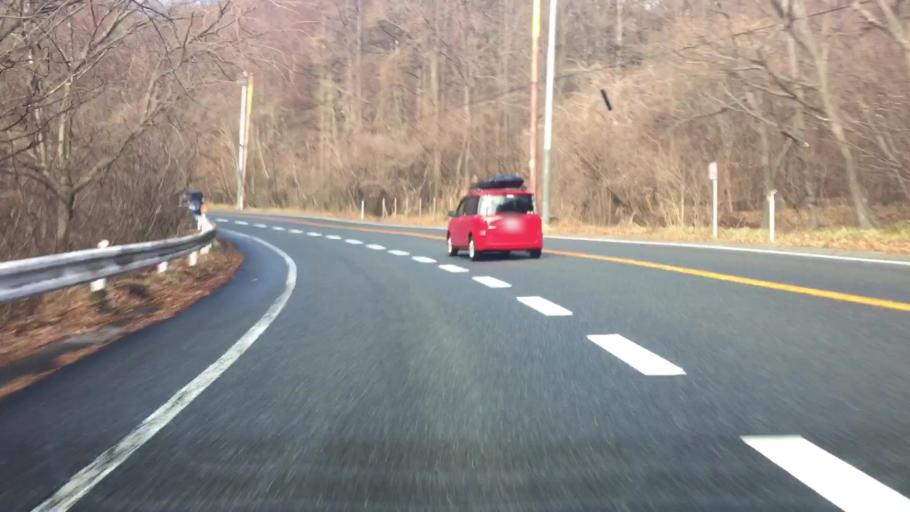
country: JP
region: Nagano
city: Saku
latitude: 36.3046
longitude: 138.6680
